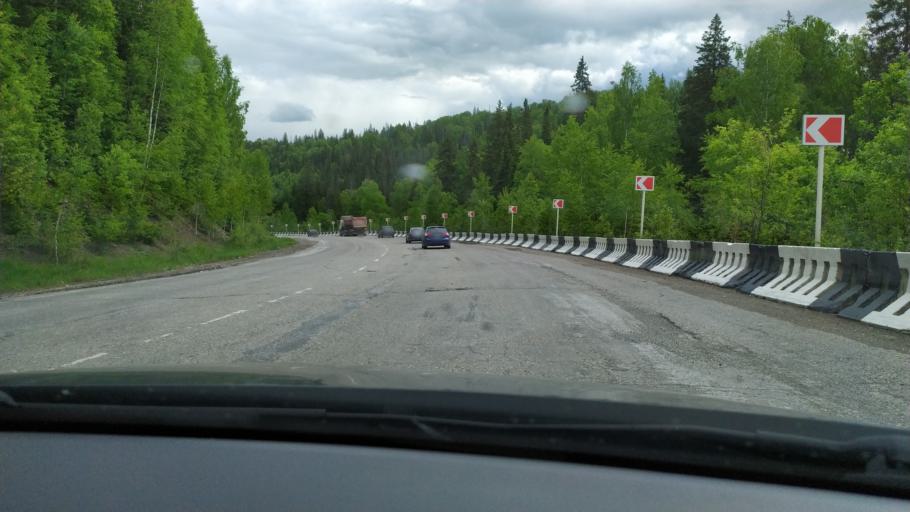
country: RU
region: Perm
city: Gremyachinsk
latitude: 58.4420
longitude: 57.8684
